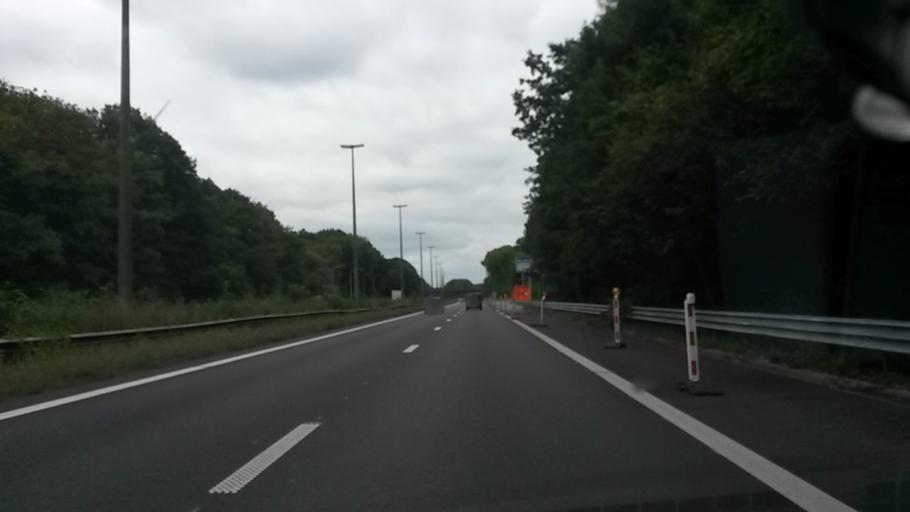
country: BE
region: Wallonia
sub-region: Province du Hainaut
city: La Louviere
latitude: 50.5020
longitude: 4.1873
